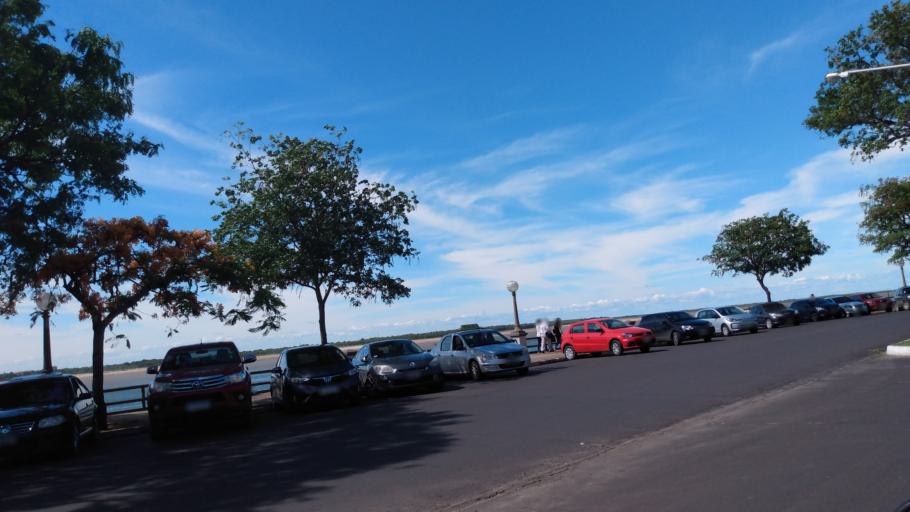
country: AR
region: Corrientes
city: Corrientes
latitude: -27.4618
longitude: -58.8422
